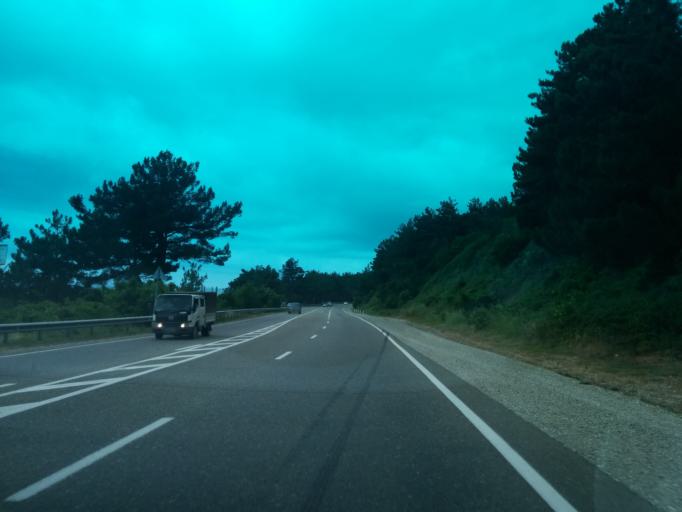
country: RU
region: Krasnodarskiy
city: Ol'ginka
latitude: 44.1843
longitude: 38.9245
